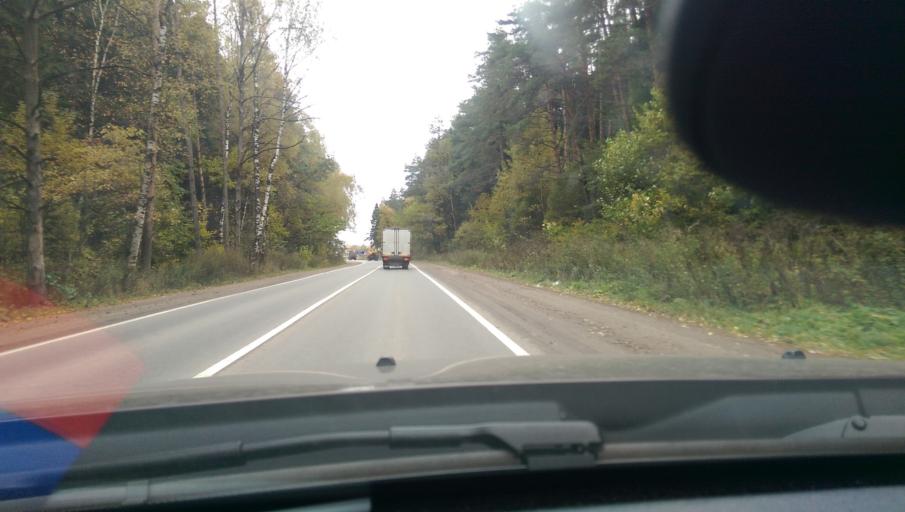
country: RU
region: Moskovskaya
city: Pirogovskiy
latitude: 55.9938
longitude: 37.7275
